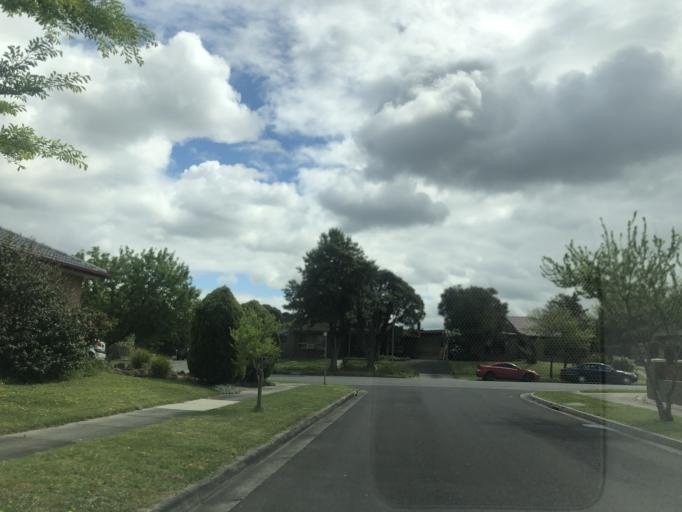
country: AU
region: Victoria
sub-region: Casey
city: Endeavour Hills
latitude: -37.9671
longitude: 145.2390
